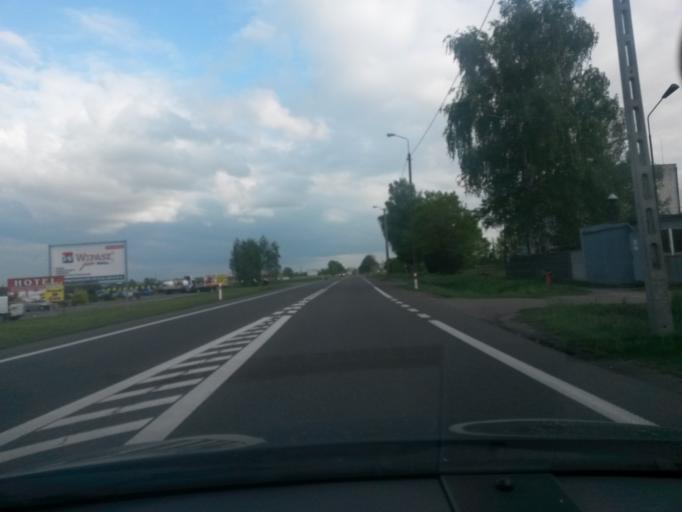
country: PL
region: Masovian Voivodeship
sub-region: Powiat plocki
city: Drobin
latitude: 52.7334
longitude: 20.0001
